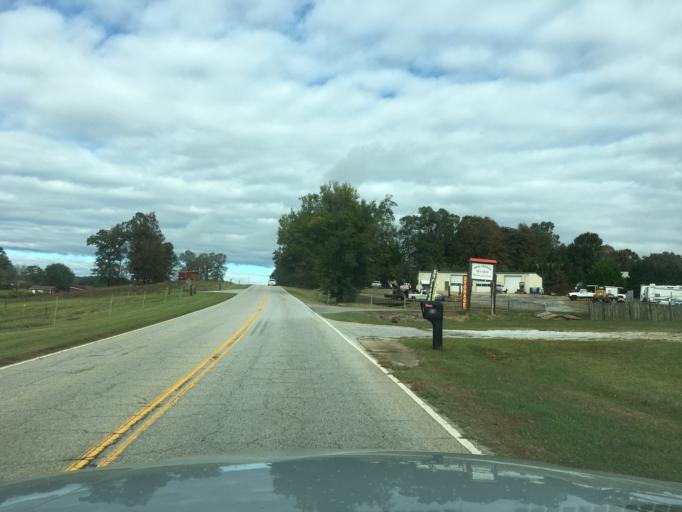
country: US
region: South Carolina
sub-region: Greenville County
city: Greer
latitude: 35.0113
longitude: -82.2586
